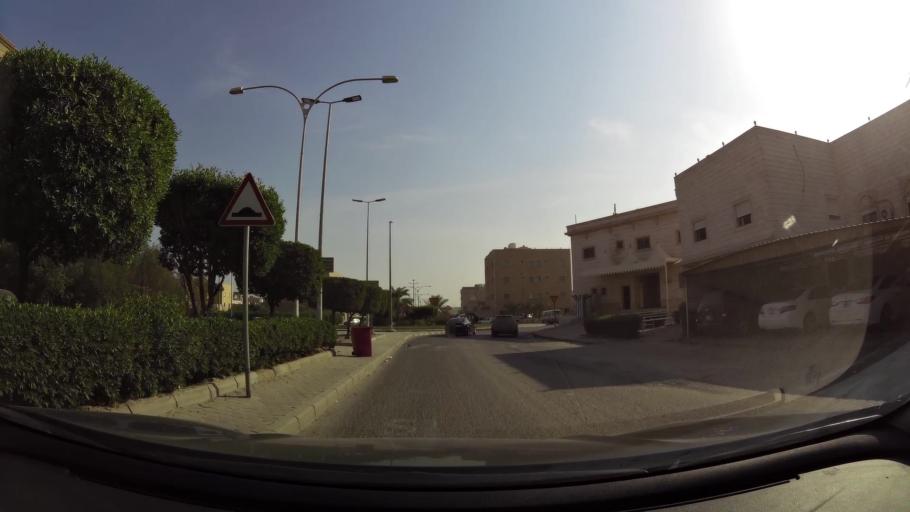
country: KW
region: Al Ahmadi
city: Ar Riqqah
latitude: 29.1510
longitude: 48.1052
